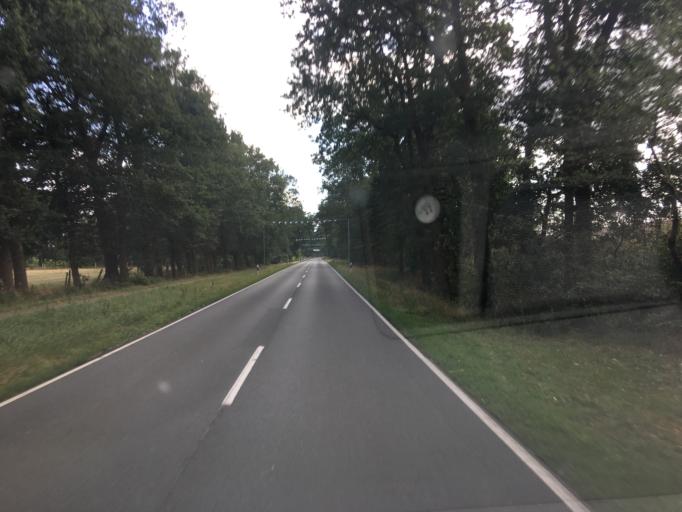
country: DE
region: Lower Saxony
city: Friesoythe
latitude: 53.0725
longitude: 7.8458
